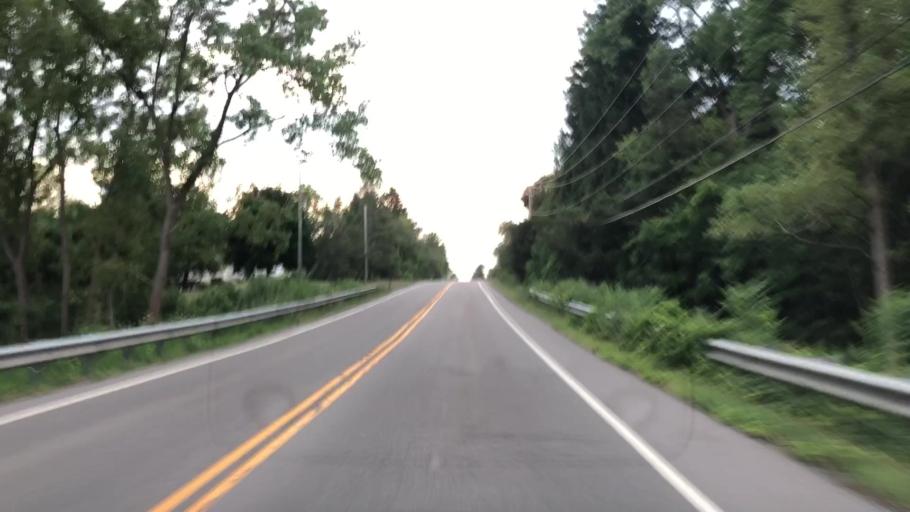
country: US
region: New York
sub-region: Erie County
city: Elma Center
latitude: 42.8390
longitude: -78.6661
